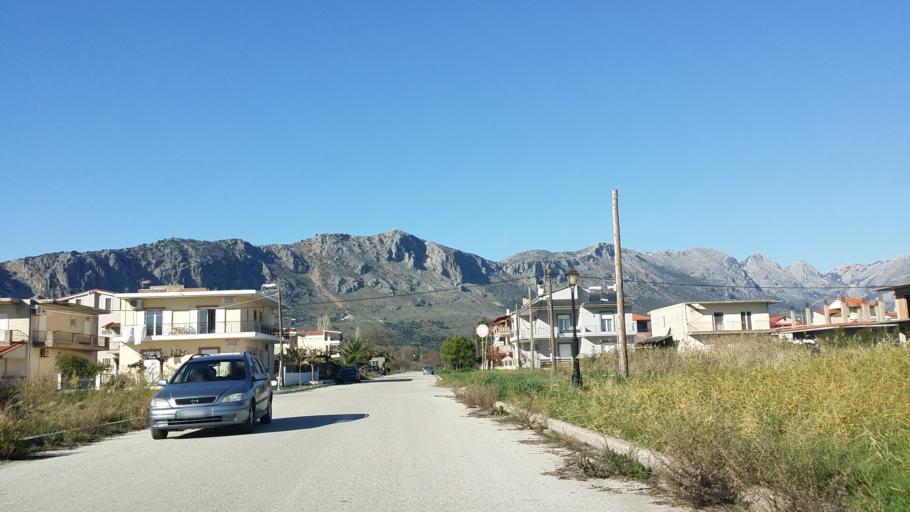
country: GR
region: West Greece
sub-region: Nomos Aitolias kai Akarnanias
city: Kandila
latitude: 38.6707
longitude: 20.9496
